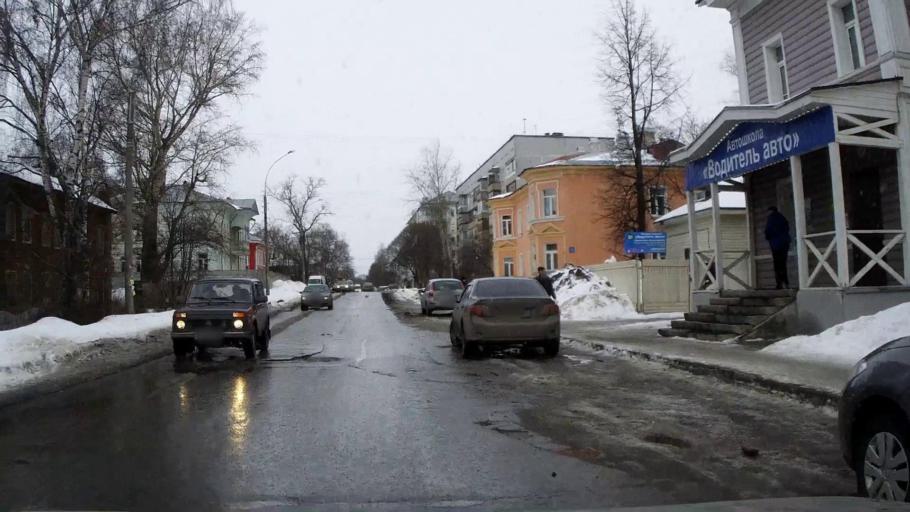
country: RU
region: Vologda
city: Vologda
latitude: 59.2261
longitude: 39.8982
